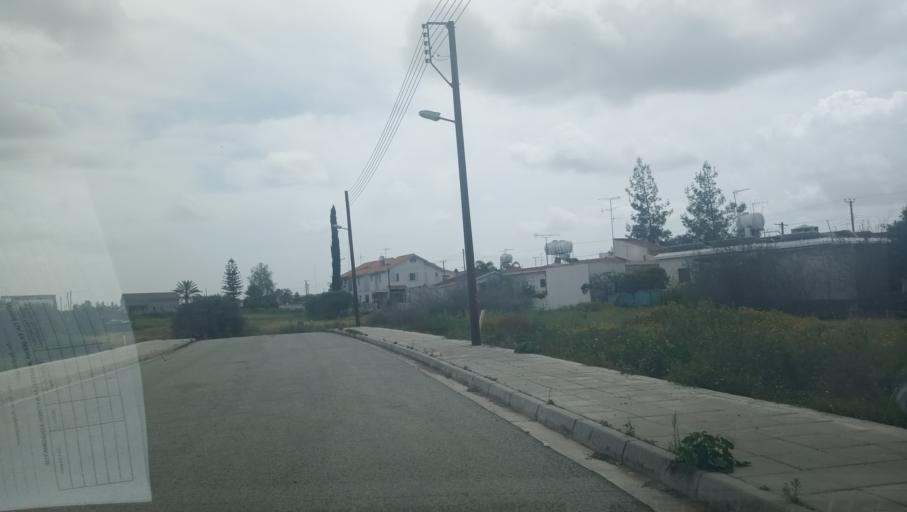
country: CY
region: Lefkosia
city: Pano Deftera
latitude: 35.0758
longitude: 33.2637
